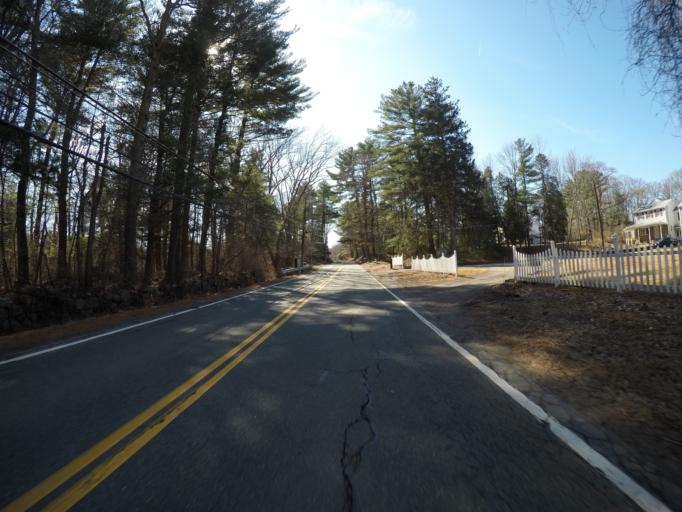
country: US
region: Massachusetts
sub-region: Norfolk County
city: Stoughton
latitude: 42.0933
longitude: -71.1350
